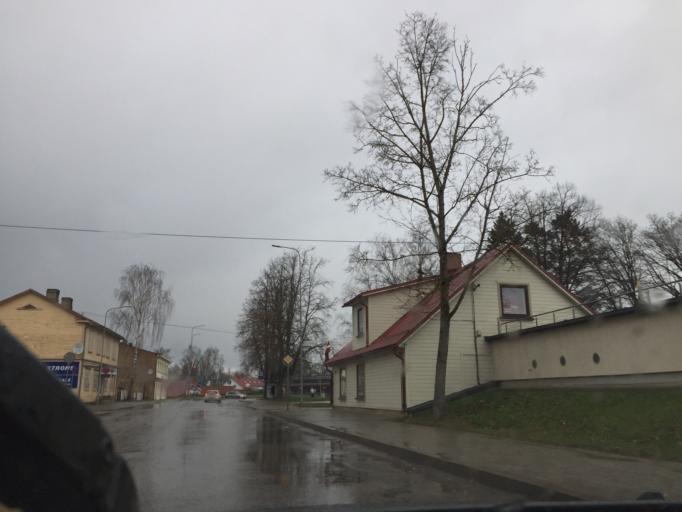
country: LV
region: Valmieras Rajons
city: Valmiera
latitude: 57.5328
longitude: 25.4250
